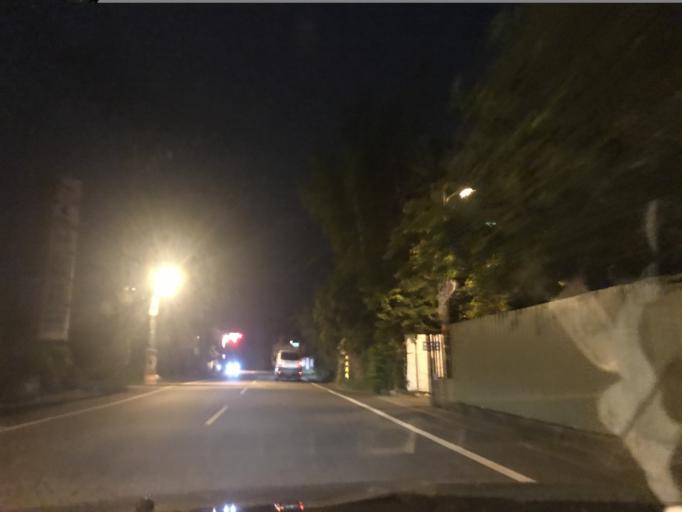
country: TW
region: Taiwan
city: Daxi
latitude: 24.9363
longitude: 121.2175
